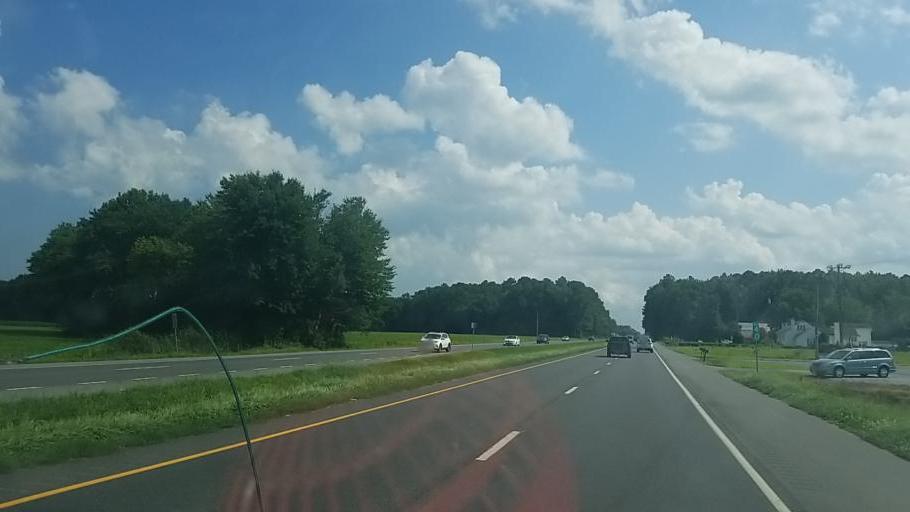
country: US
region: Delaware
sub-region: Sussex County
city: Selbyville
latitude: 38.5091
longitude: -75.2382
